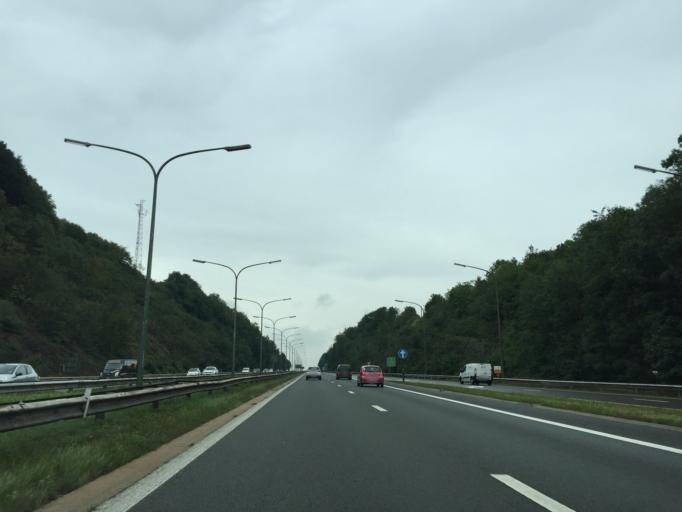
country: BE
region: Wallonia
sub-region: Province de Liege
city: Dison
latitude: 50.5968
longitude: 5.8452
